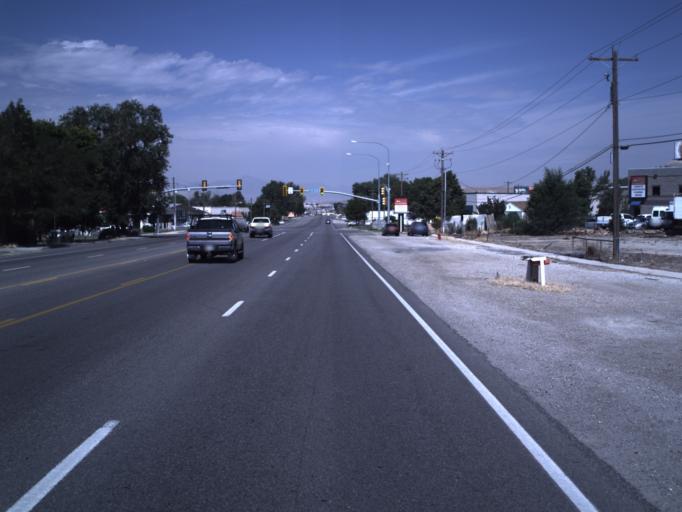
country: US
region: Utah
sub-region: Utah County
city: Lehi
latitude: 40.4055
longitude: -111.8592
